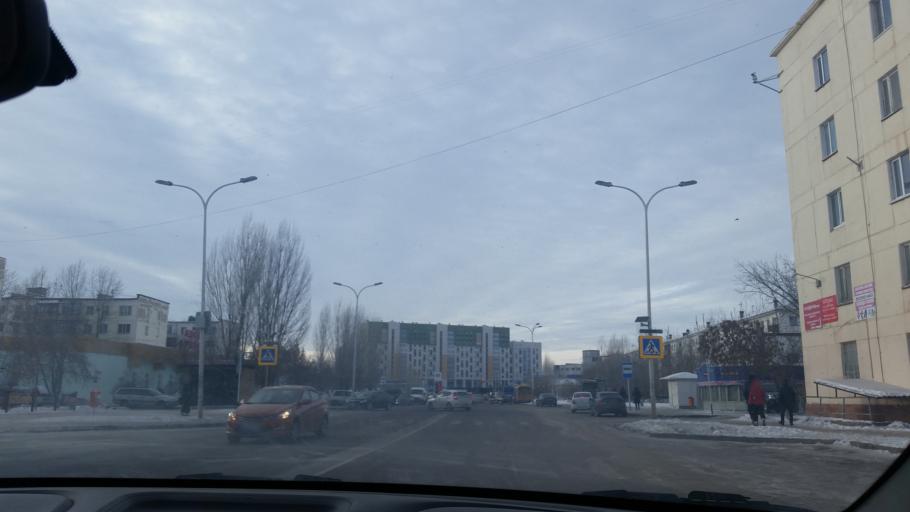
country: KZ
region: Astana Qalasy
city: Astana
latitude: 51.1462
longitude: 71.4643
